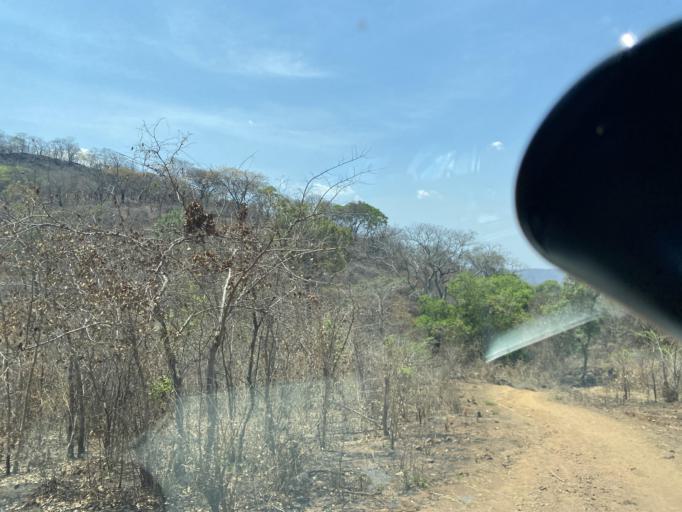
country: ZM
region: Lusaka
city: Kafue
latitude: -15.8017
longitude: 28.4504
